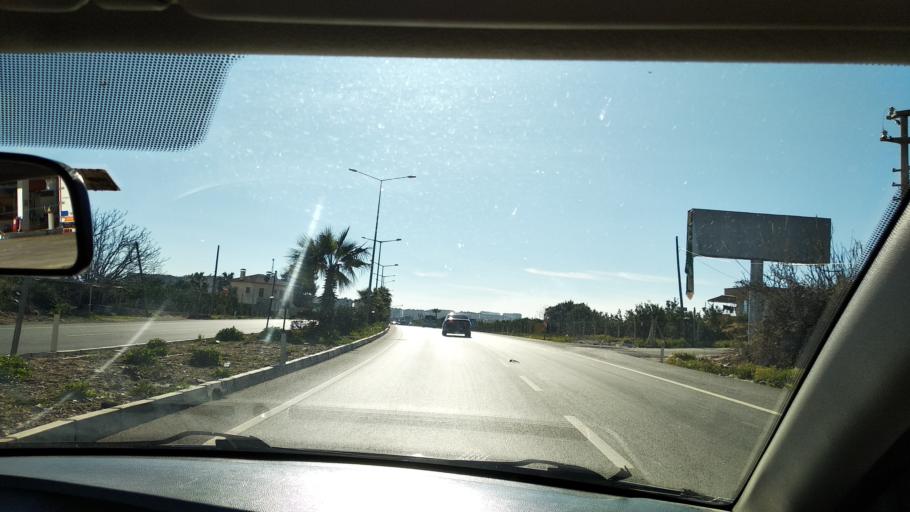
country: TR
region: Mersin
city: Tomuk
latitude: 36.6659
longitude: 34.3990
